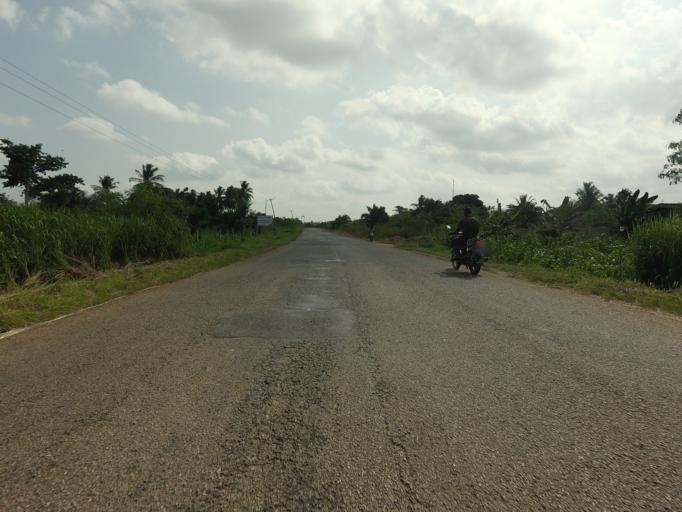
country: GH
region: Volta
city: Ho
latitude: 6.4159
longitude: 0.7515
